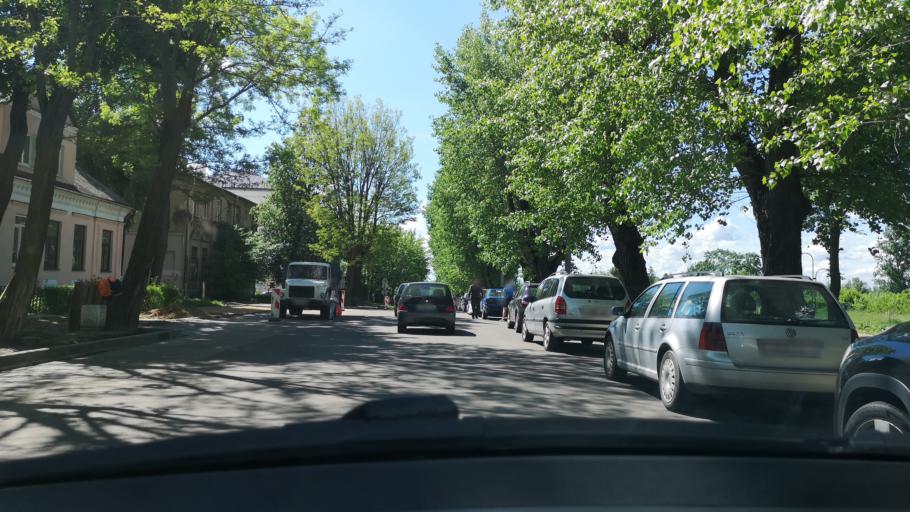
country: BY
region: Brest
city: Brest
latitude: 52.0853
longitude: 23.6868
